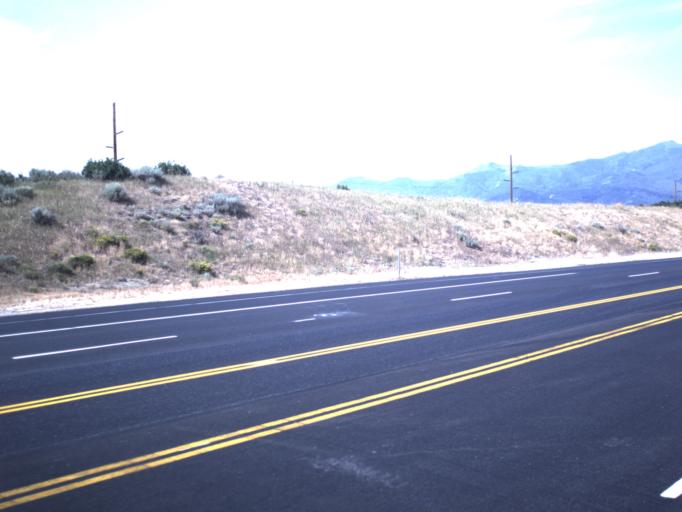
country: US
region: Utah
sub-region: Summit County
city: Kamas
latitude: 40.6341
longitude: -111.3780
